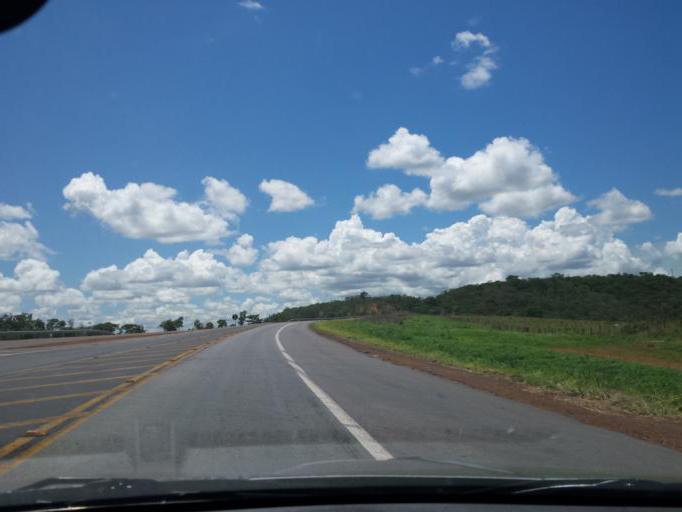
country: BR
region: Goias
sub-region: Cristalina
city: Cristalina
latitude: -16.6296
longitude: -47.7396
